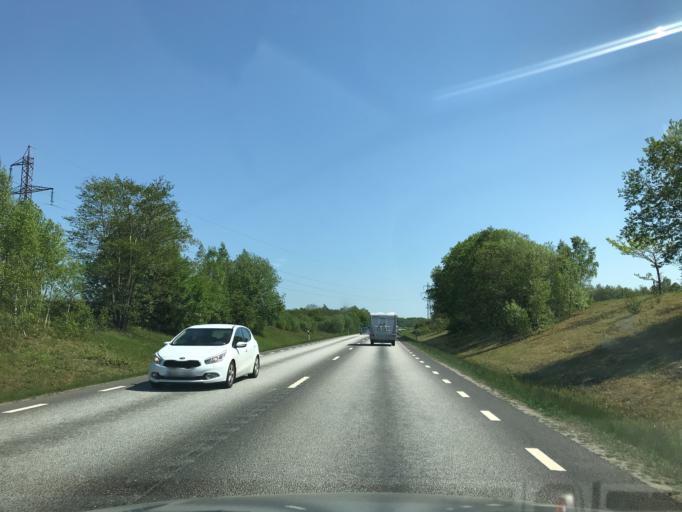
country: SE
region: Skane
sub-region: Klippans Kommun
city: Klippan
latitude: 56.1180
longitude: 13.1300
